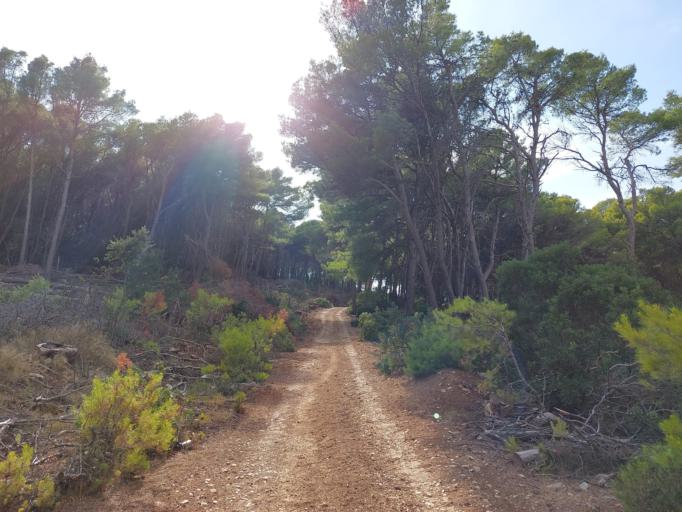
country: HR
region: Dubrovacko-Neretvanska
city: Smokvica
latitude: 42.7358
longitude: 16.8288
